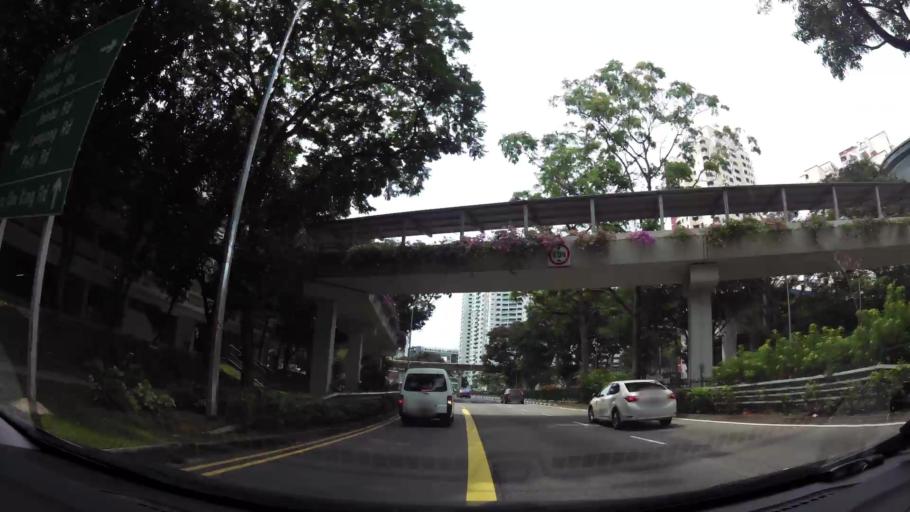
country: MY
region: Johor
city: Johor Bahru
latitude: 1.3811
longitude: 103.7646
